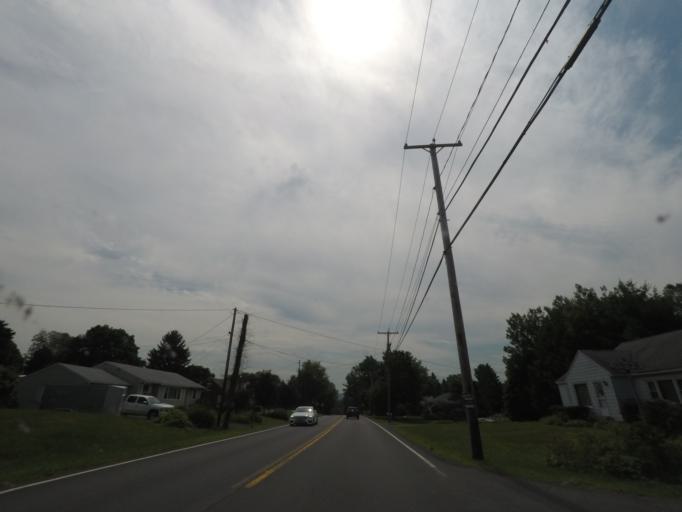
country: US
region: New York
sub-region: Rensselaer County
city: Wynantskill
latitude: 42.7597
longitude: -73.6204
